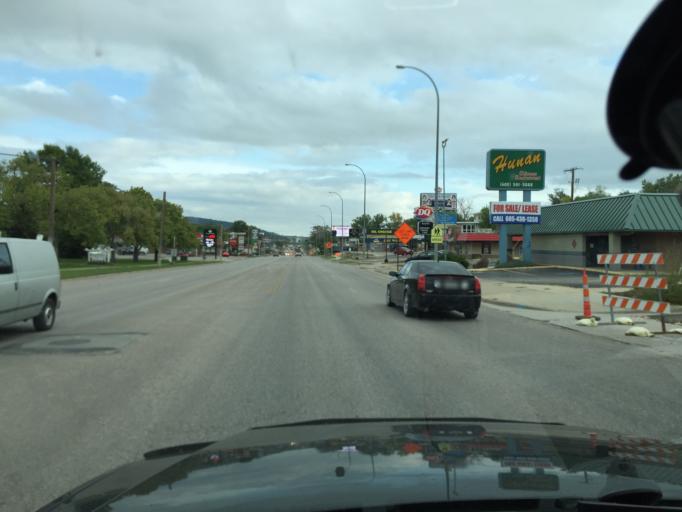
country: US
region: South Dakota
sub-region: Pennington County
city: Rapid City
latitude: 44.0684
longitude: -103.2324
